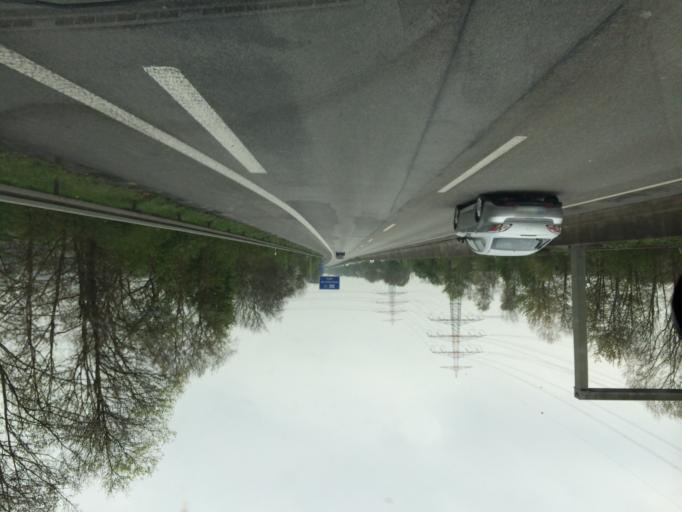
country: DE
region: North Rhine-Westphalia
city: Waltrop
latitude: 51.5799
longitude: 7.3658
